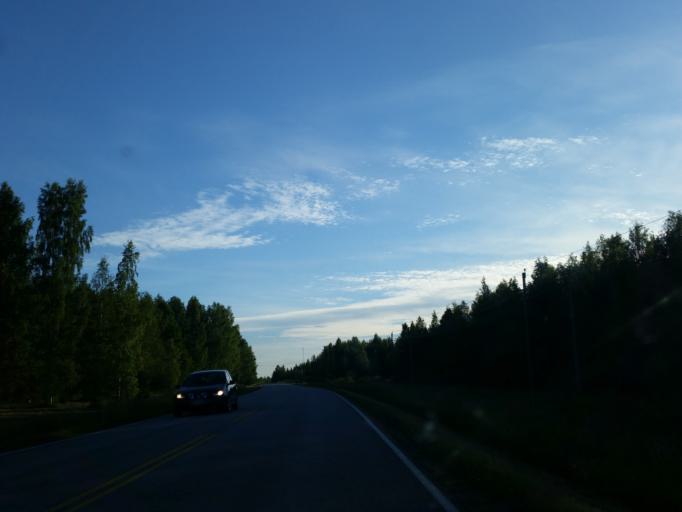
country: FI
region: Northern Savo
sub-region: Kuopio
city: Karttula
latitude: 62.9038
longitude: 26.9585
